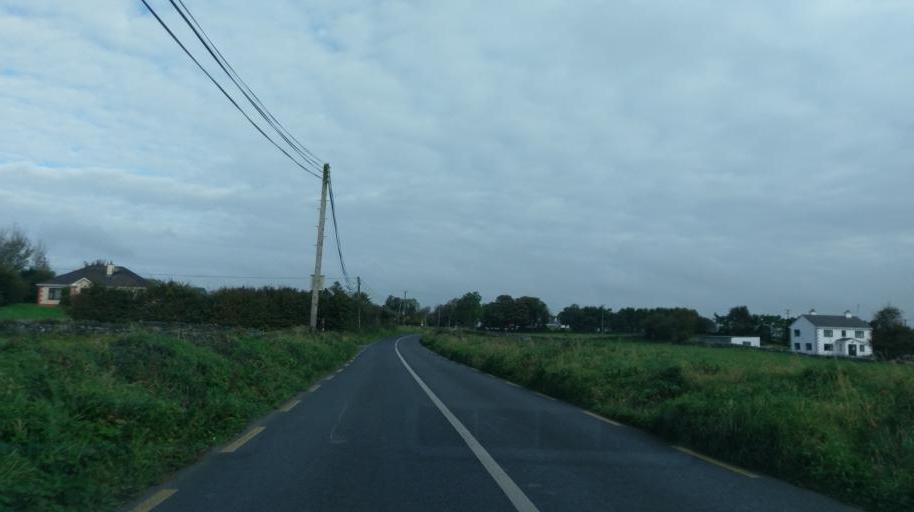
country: IE
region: Connaught
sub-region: County Galway
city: Athenry
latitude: 53.3221
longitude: -8.7277
